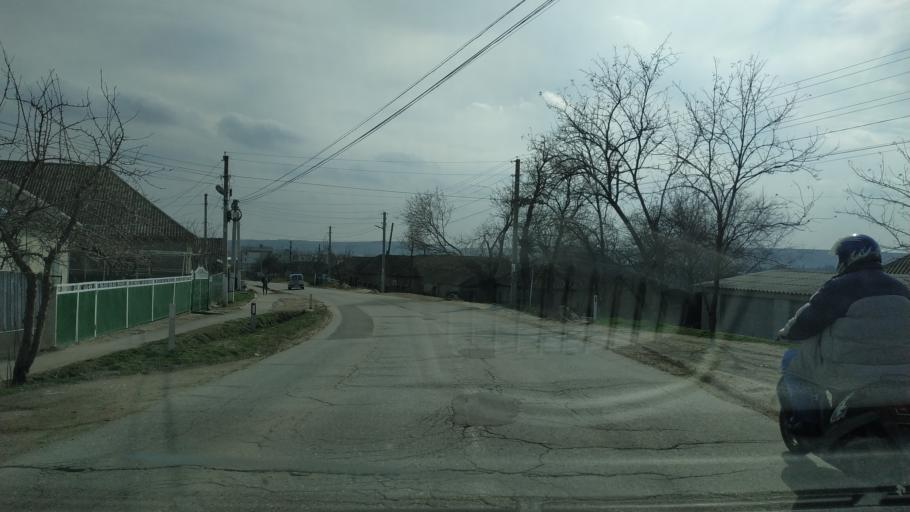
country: MD
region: Gagauzia
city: Vulcanesti
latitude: 45.6920
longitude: 28.4048
